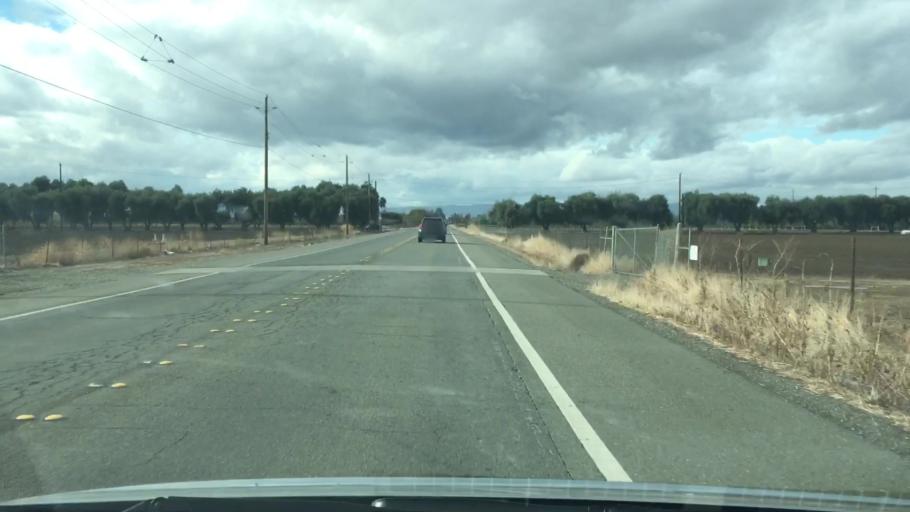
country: US
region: California
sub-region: Yolo County
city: Davis
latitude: 38.5397
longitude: -121.7884
